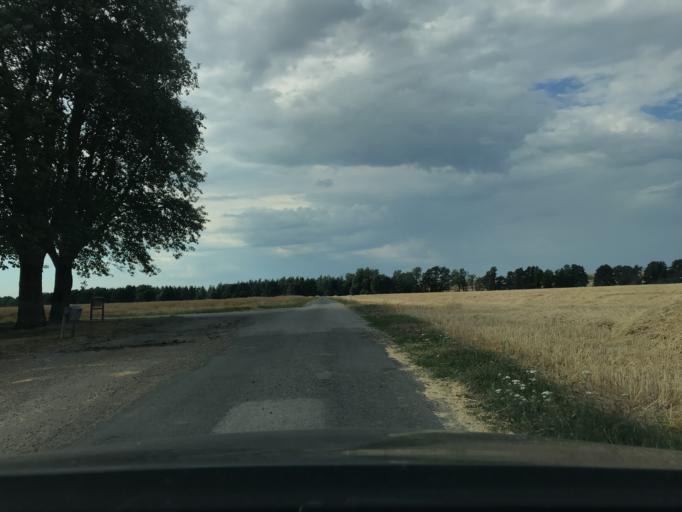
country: SE
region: Skane
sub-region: Simrishamns Kommun
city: Kivik
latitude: 55.5380
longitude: 14.1542
